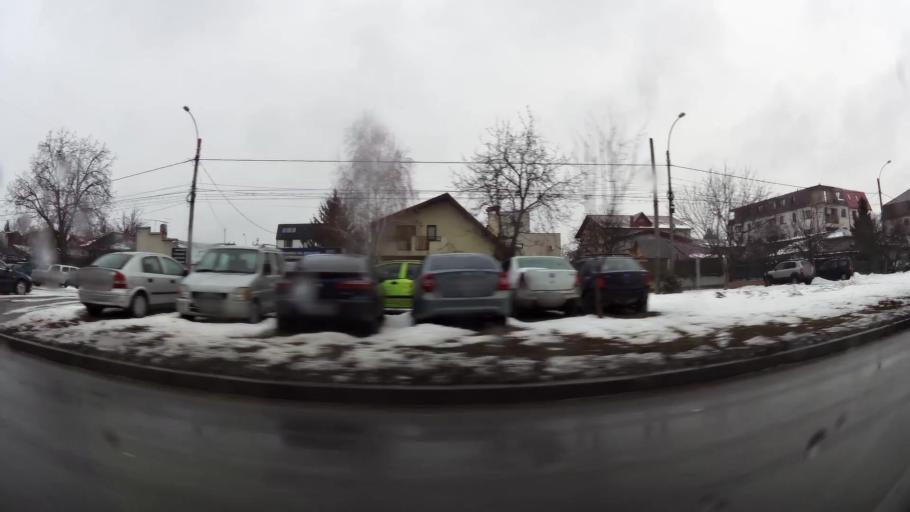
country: RO
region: Ilfov
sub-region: Comuna Chiajna
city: Rosu
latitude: 44.4885
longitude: 26.0255
